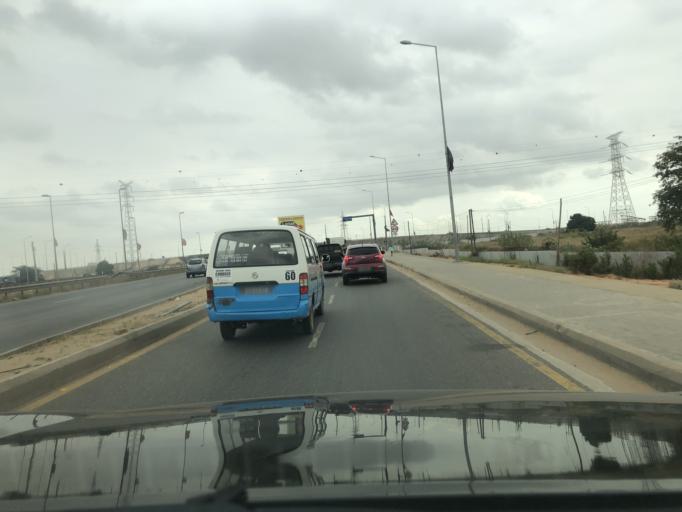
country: AO
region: Luanda
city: Luanda
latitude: -8.9730
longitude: 13.2579
